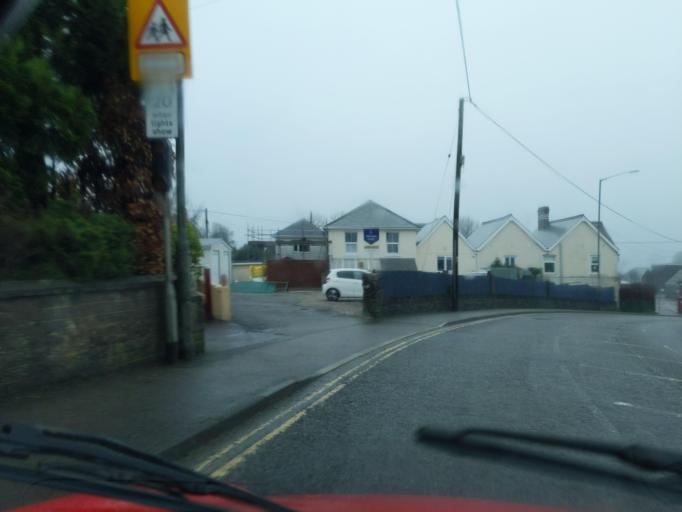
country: GB
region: England
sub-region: Cornwall
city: Callington
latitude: 50.5004
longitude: -4.3123
